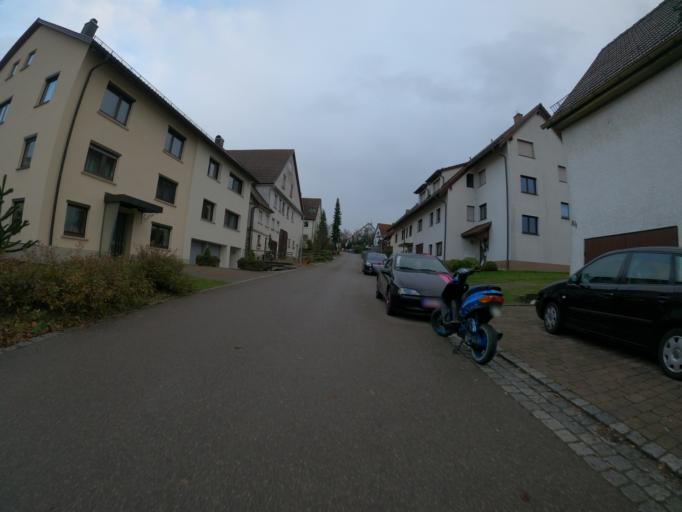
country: DE
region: Baden-Wuerttemberg
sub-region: Regierungsbezirk Stuttgart
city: Waschenbeuren
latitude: 48.7567
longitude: 9.6865
